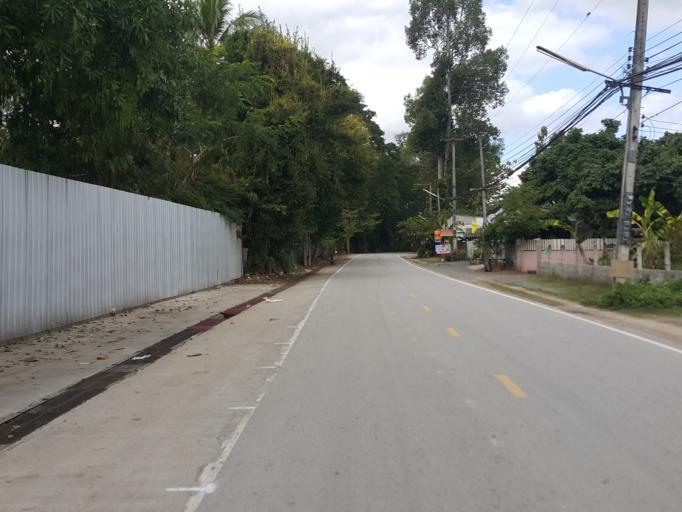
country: TH
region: Chiang Mai
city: San Sai
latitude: 18.8666
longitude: 99.1378
